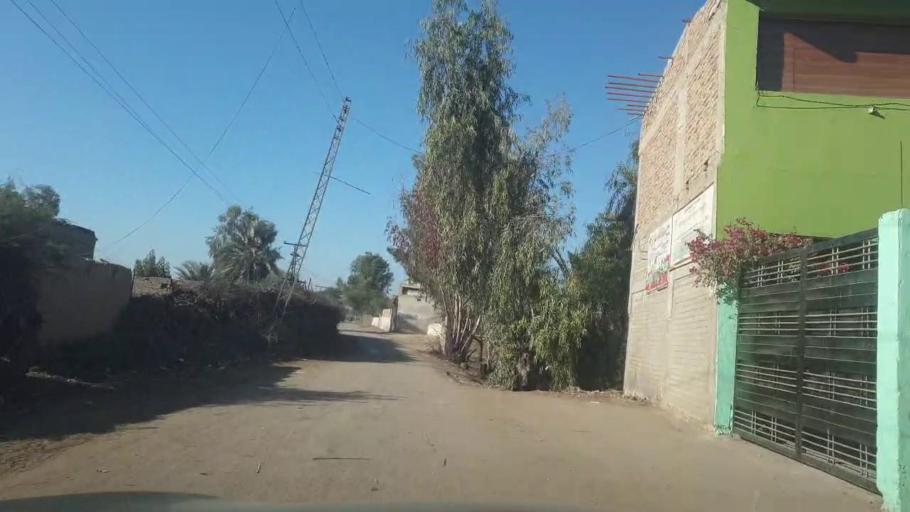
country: PK
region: Sindh
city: Adilpur
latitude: 27.9299
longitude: 69.2559
